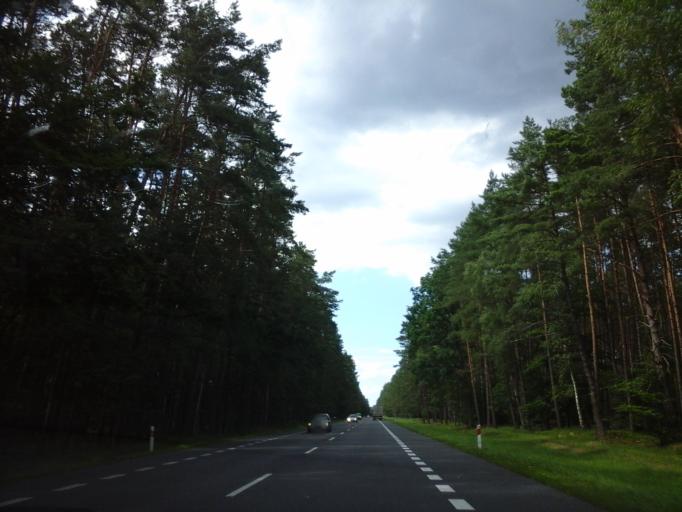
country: PL
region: West Pomeranian Voivodeship
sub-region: Powiat goleniowski
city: Przybiernow
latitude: 53.7020
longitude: 14.7848
